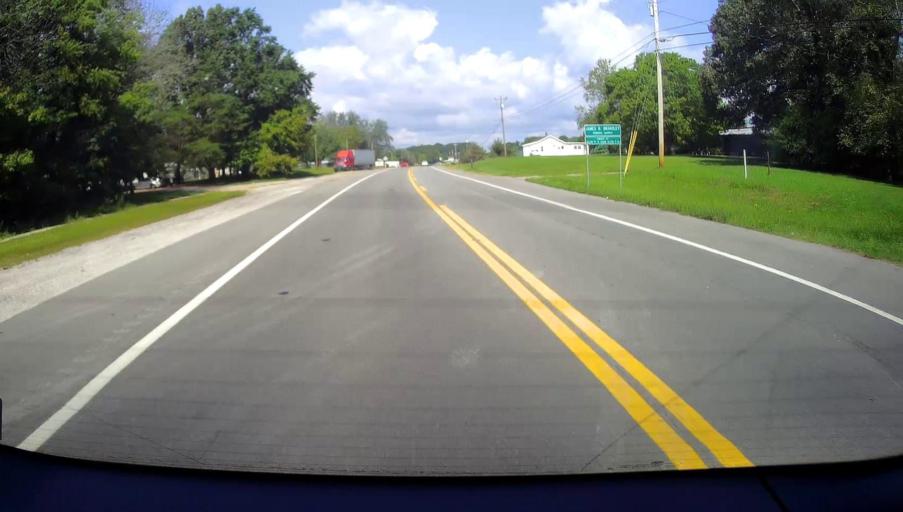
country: US
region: Tennessee
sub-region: Coffee County
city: Manchester
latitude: 35.4999
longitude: -86.1114
